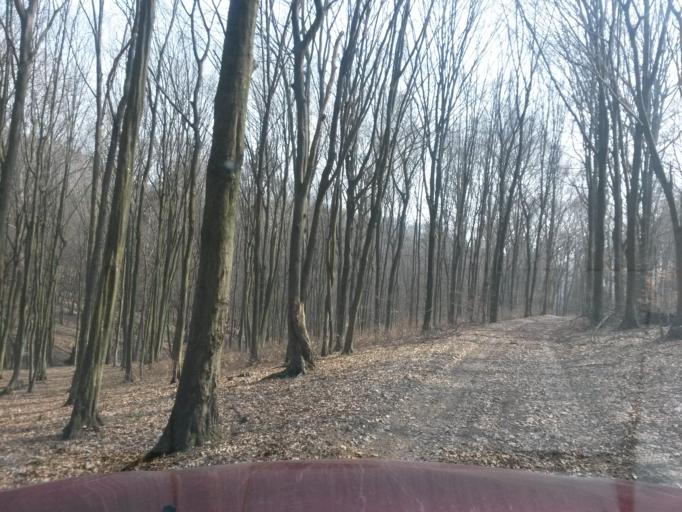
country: SK
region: Presovsky
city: Sabinov
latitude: 48.9700
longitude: 21.1010
